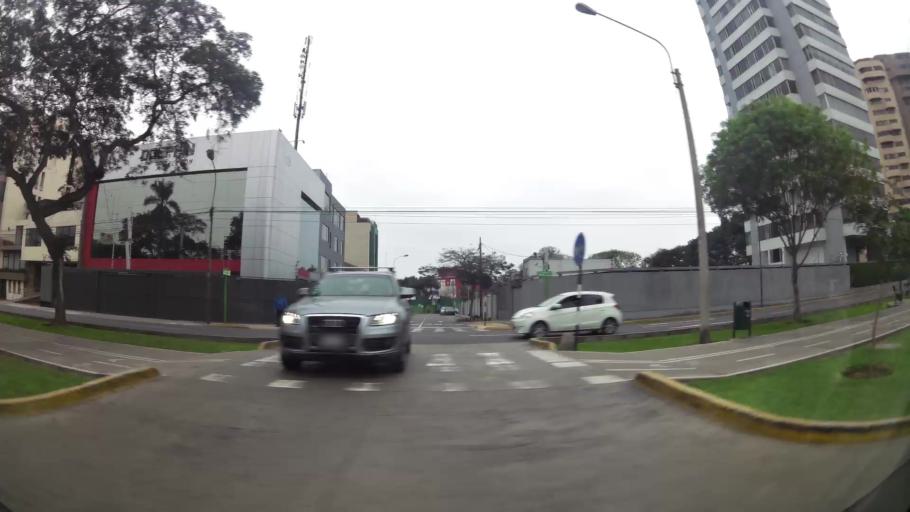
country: PE
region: Lima
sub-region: Lima
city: San Isidro
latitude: -12.1044
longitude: -77.0314
